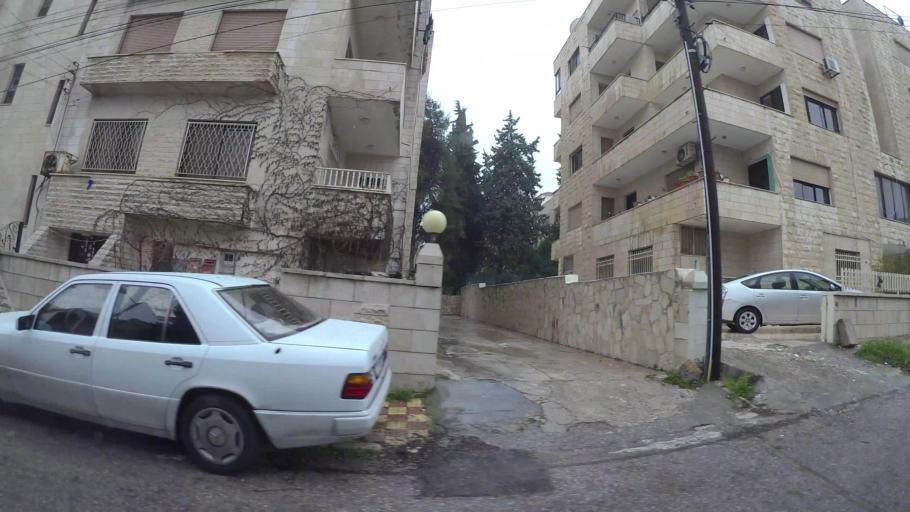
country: JO
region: Amman
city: Al Jubayhah
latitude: 31.9665
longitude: 35.8794
